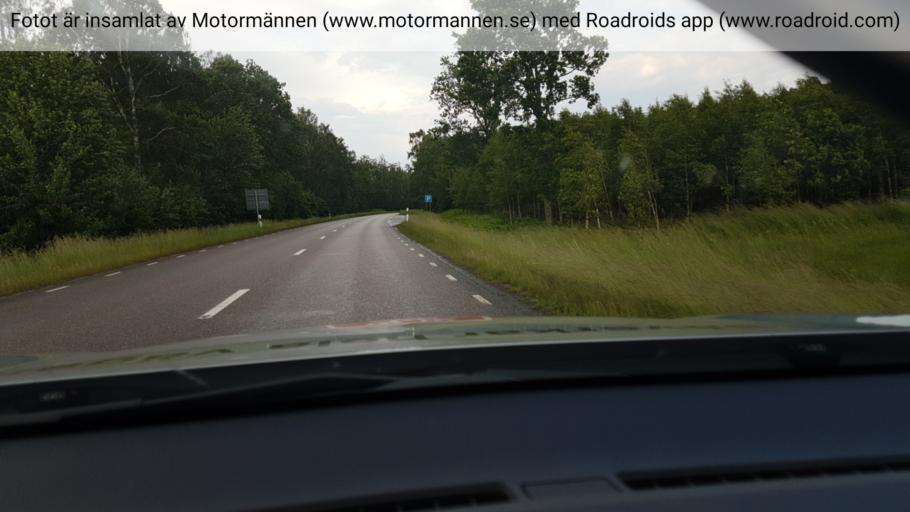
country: SE
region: Vaestra Goetaland
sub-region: Hjo Kommun
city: Hjo
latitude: 58.2521
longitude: 14.2348
